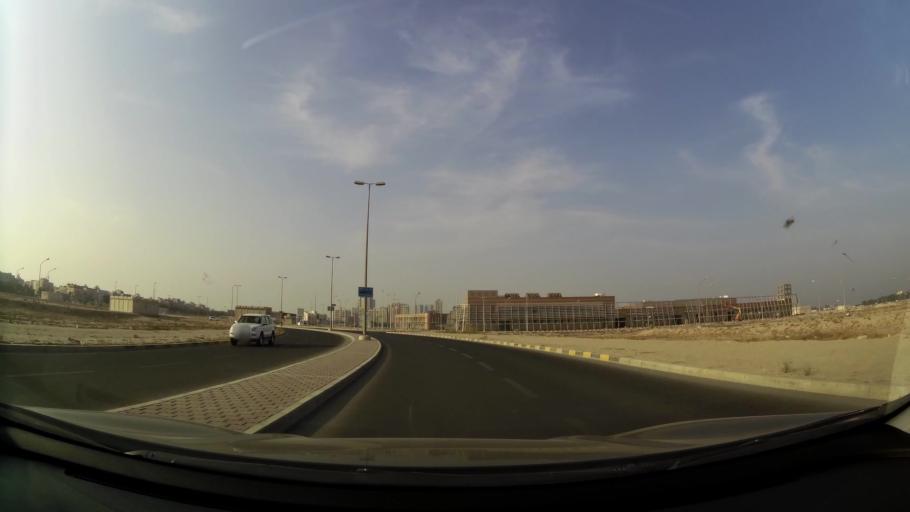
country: KW
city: Al Funaytis
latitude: 29.2401
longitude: 48.0866
